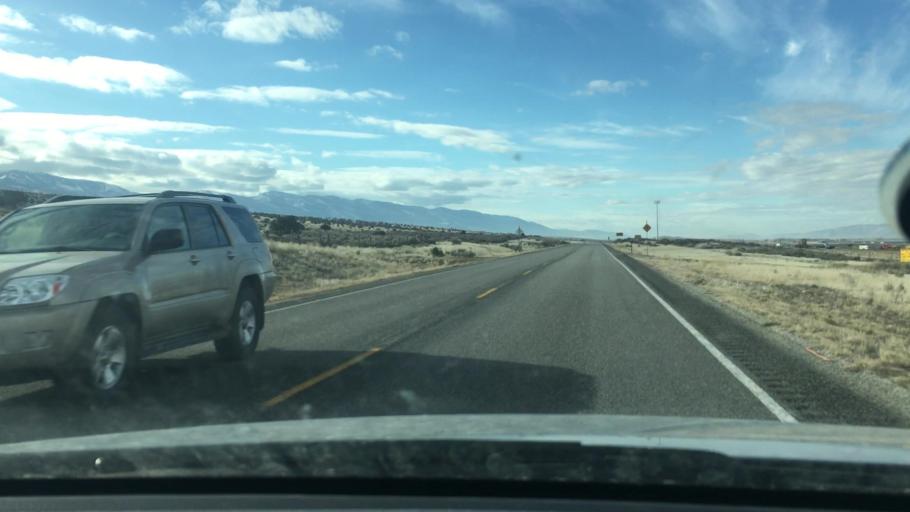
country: US
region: Utah
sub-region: Sanpete County
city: Moroni
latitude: 39.4499
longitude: -111.5436
